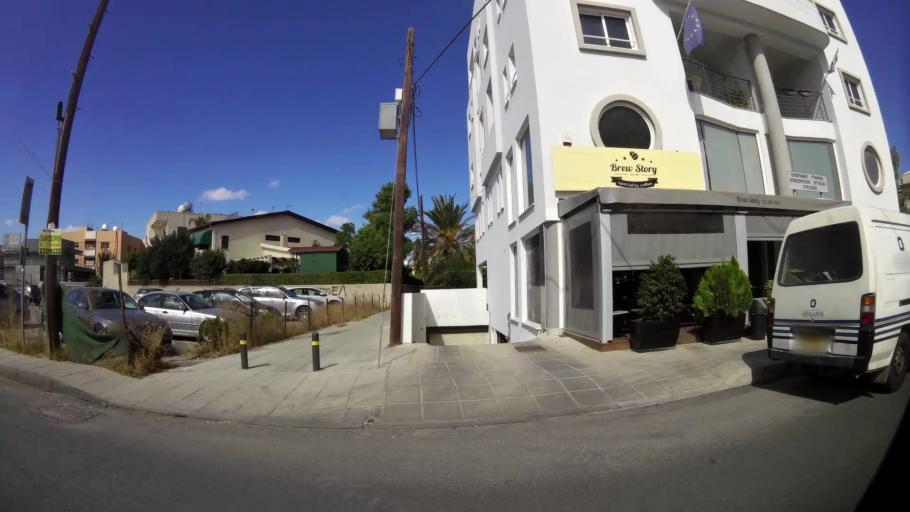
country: CY
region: Lefkosia
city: Nicosia
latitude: 35.1402
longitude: 33.3684
